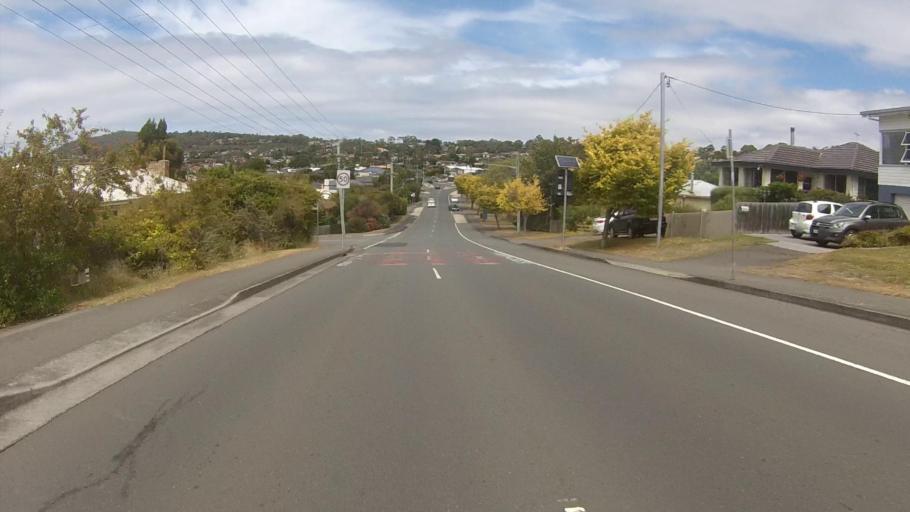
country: AU
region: Tasmania
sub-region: Kingborough
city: Blackmans Bay
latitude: -42.9976
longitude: 147.3223
